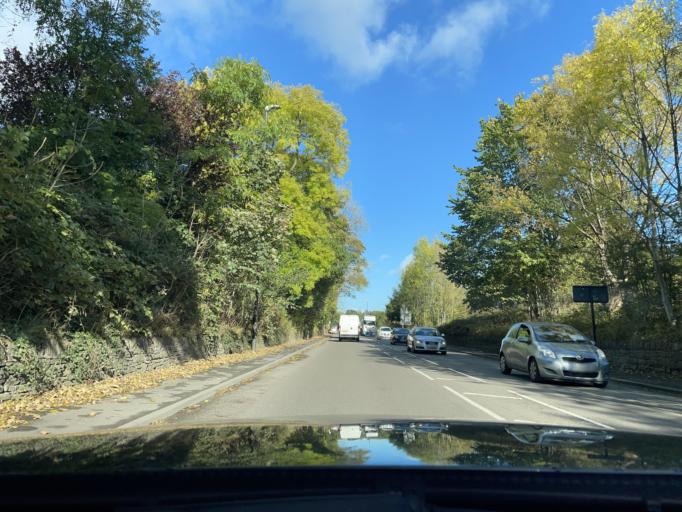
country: GB
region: England
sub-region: Derbyshire
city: Whaley Bridge
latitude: 53.3423
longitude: -1.9855
